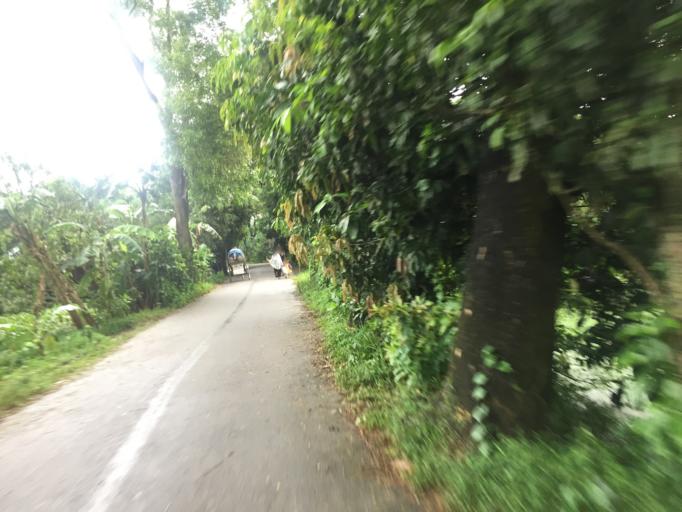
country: BD
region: Dhaka
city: Narayanganj
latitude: 23.5407
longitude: 90.4721
